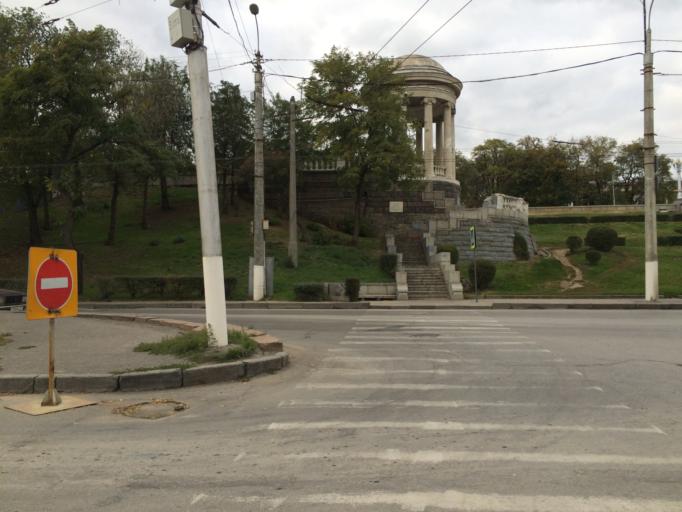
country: RU
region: Volgograd
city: Volgograd
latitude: 48.7019
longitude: 44.5193
